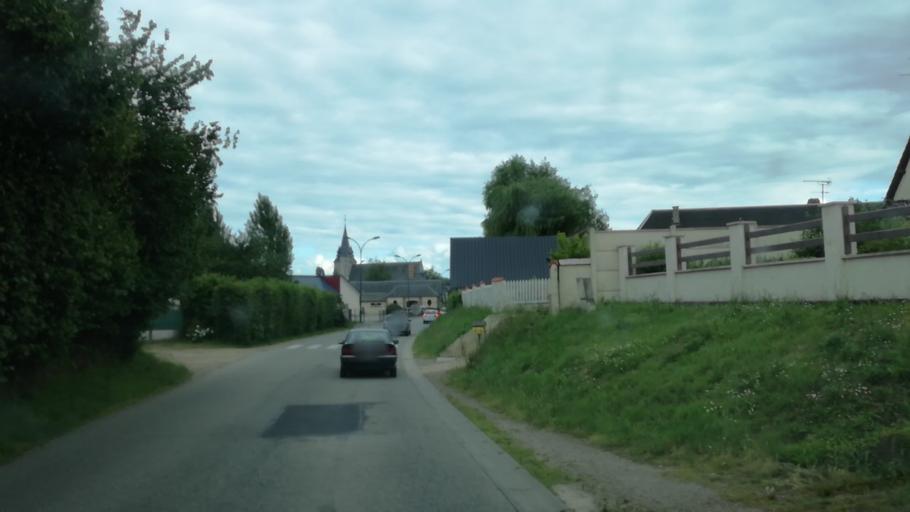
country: FR
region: Haute-Normandie
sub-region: Departement de l'Eure
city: Bourgtheroulde-Infreville
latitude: 49.2285
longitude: 0.8393
